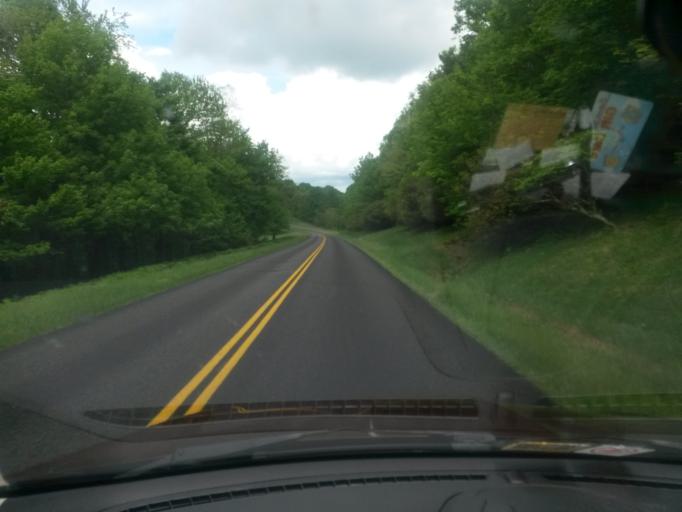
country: US
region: Virginia
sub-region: Floyd County
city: Floyd
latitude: 36.8073
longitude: -80.3563
